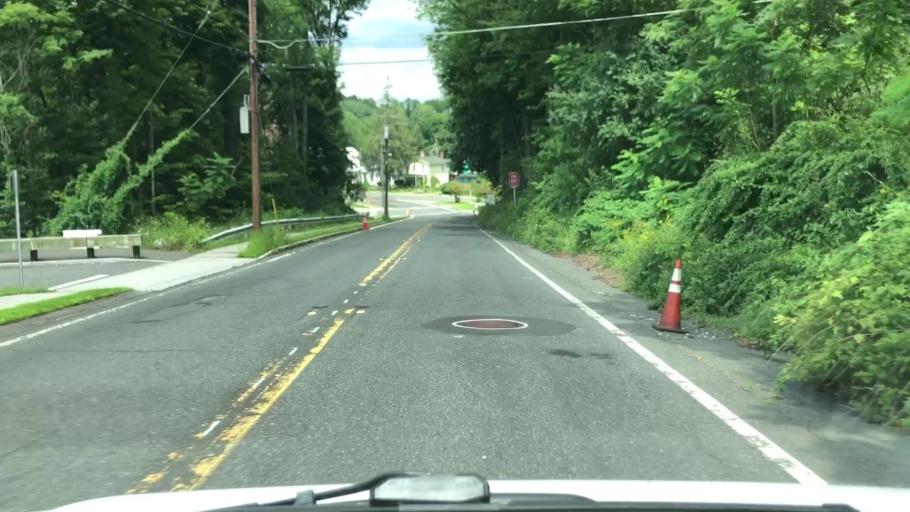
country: US
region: Massachusetts
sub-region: Franklin County
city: Conway
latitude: 42.5069
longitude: -72.6960
